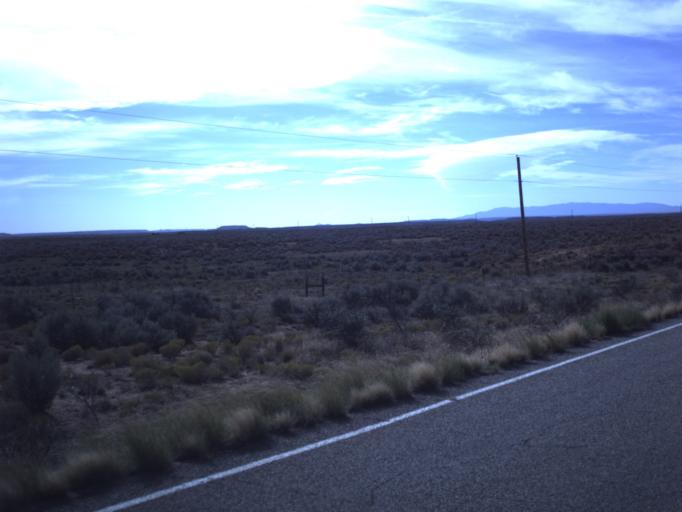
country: US
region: Utah
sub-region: San Juan County
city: Blanding
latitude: 37.4005
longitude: -109.3375
